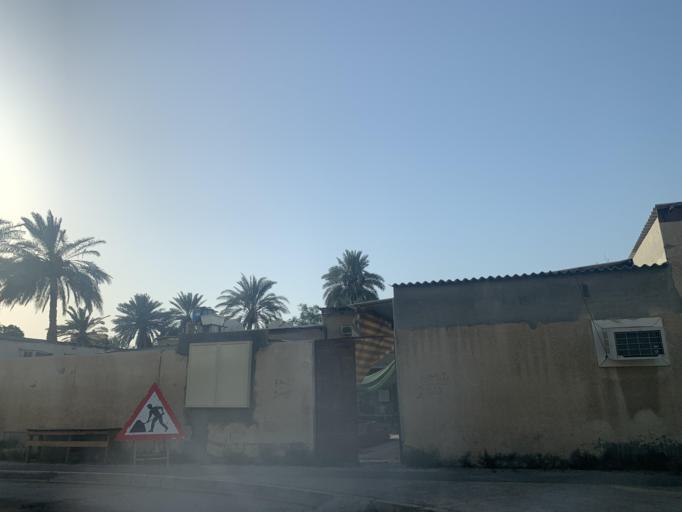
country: BH
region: Manama
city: Jidd Hafs
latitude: 26.2100
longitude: 50.4529
